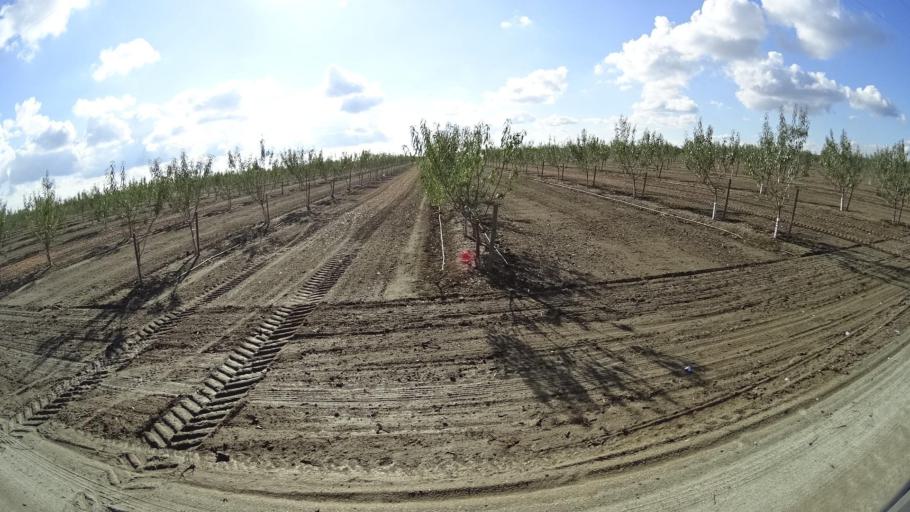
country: US
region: California
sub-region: Kern County
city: McFarland
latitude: 35.6599
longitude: -119.2304
